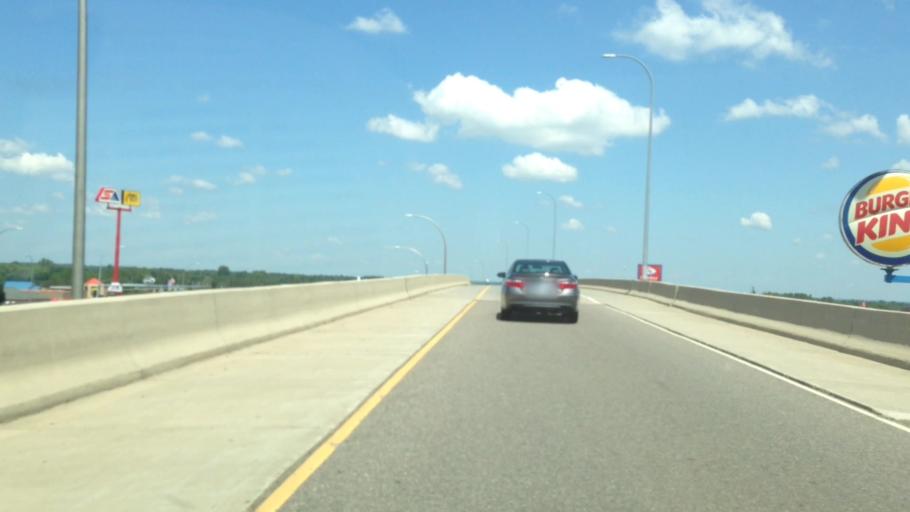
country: US
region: Minnesota
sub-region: Hennepin County
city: Rogers
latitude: 45.1980
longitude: -93.5519
